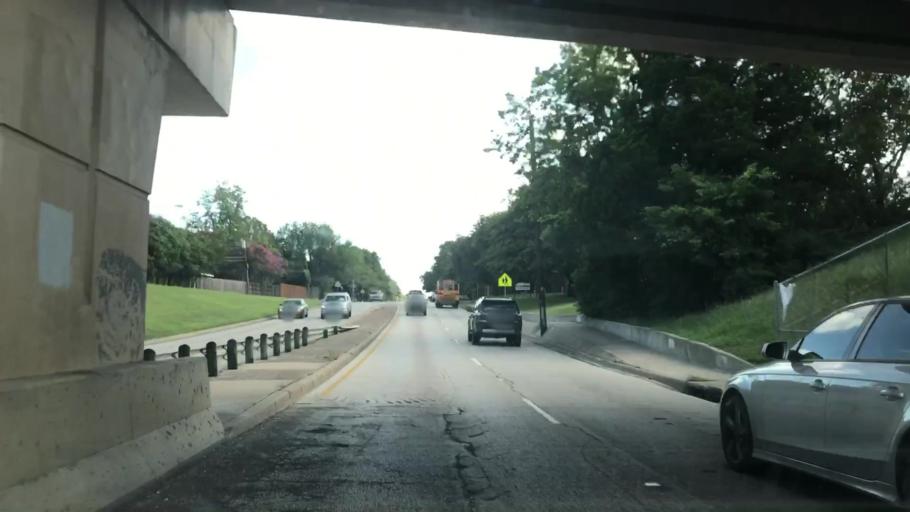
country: US
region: Texas
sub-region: Dallas County
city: Highland Park
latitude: 32.8418
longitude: -96.7614
